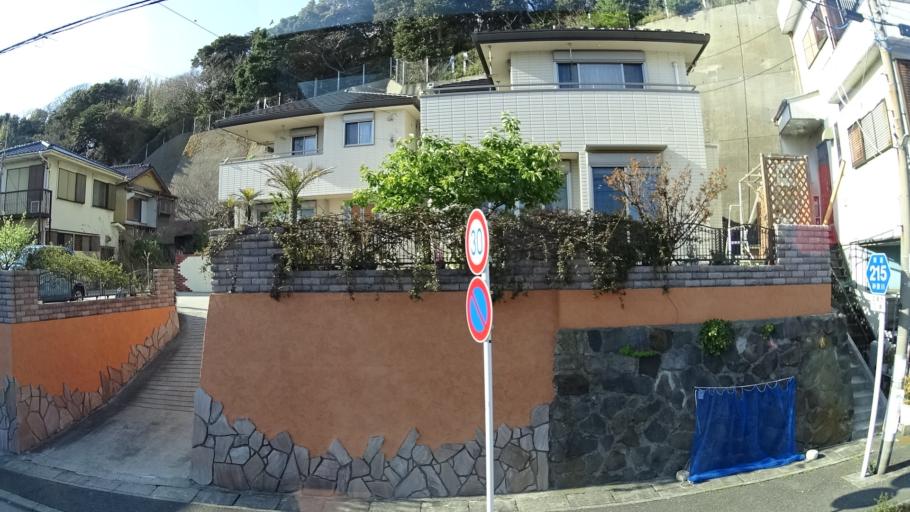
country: JP
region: Kanagawa
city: Miura
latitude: 35.1431
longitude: 139.6228
